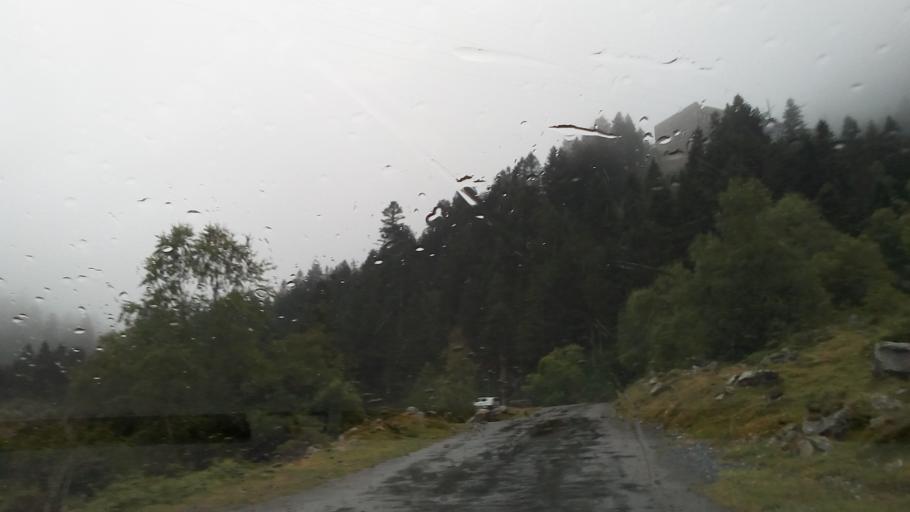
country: ES
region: Aragon
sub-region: Provincia de Huesca
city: Sallent de Gallego
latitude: 42.8891
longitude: -0.2712
